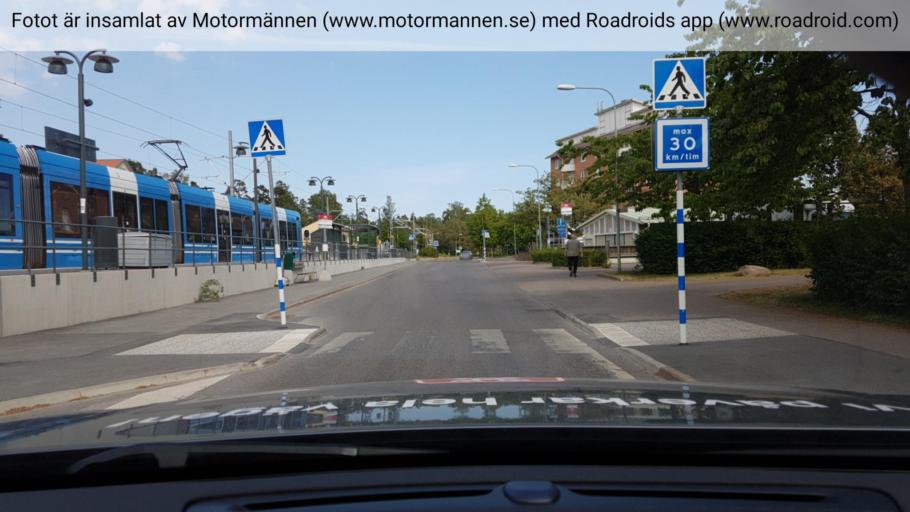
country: SE
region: Stockholm
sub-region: Lidingo
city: Brevik
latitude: 59.3482
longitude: 18.2027
